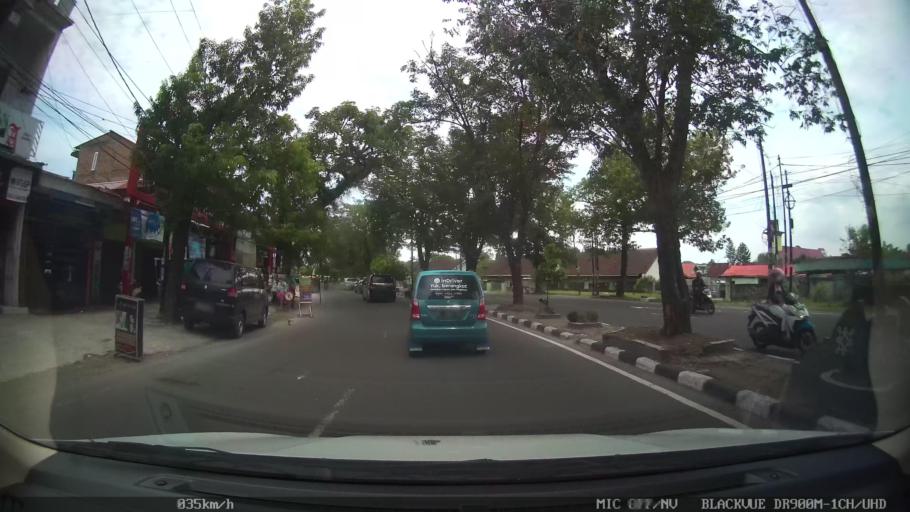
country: ID
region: North Sumatra
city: Medan
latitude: 3.5611
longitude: 98.6624
